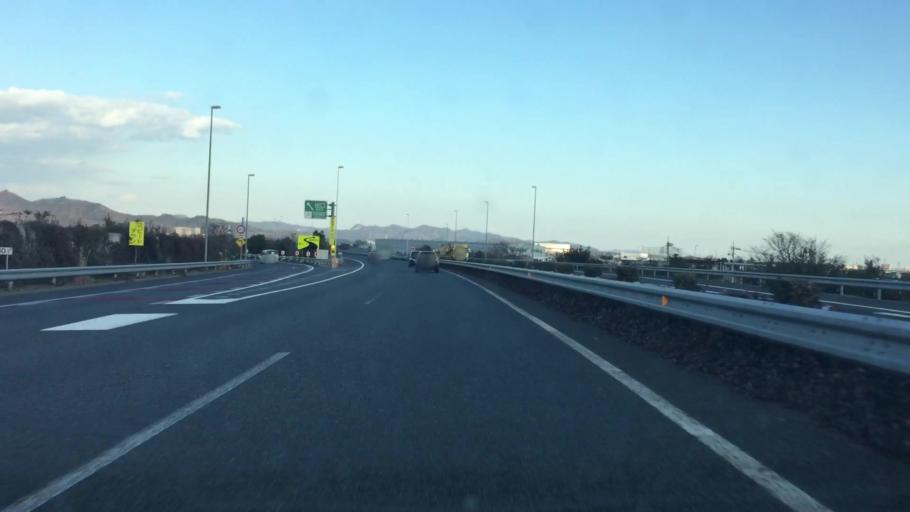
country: JP
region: Gunma
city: Ota
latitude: 36.3298
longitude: 139.3856
